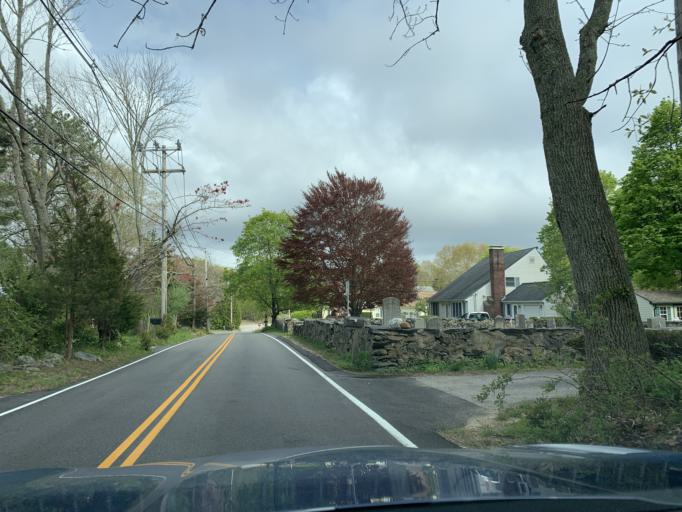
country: US
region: Rhode Island
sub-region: Washington County
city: North Kingstown
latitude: 41.6030
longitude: -71.4822
